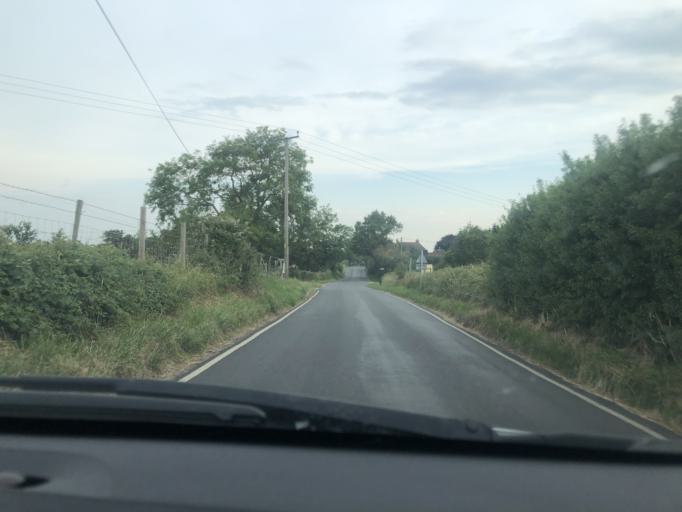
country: GB
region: England
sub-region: Kent
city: Herne Bay
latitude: 51.3347
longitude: 1.1550
